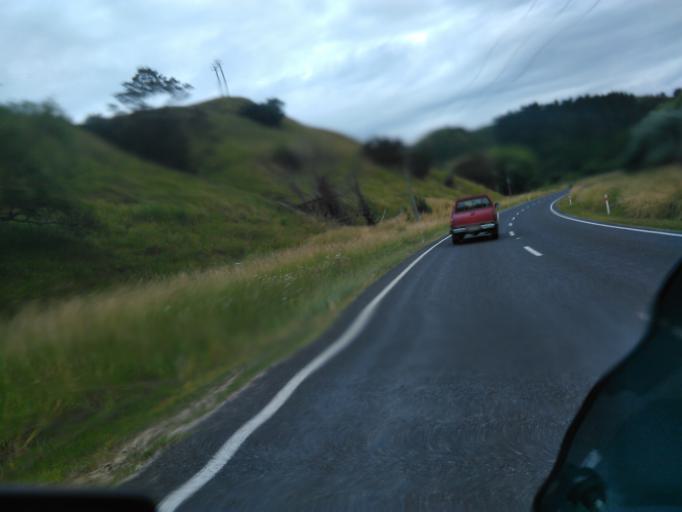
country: NZ
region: Gisborne
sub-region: Gisborne District
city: Gisborne
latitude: -38.4577
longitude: 177.7462
